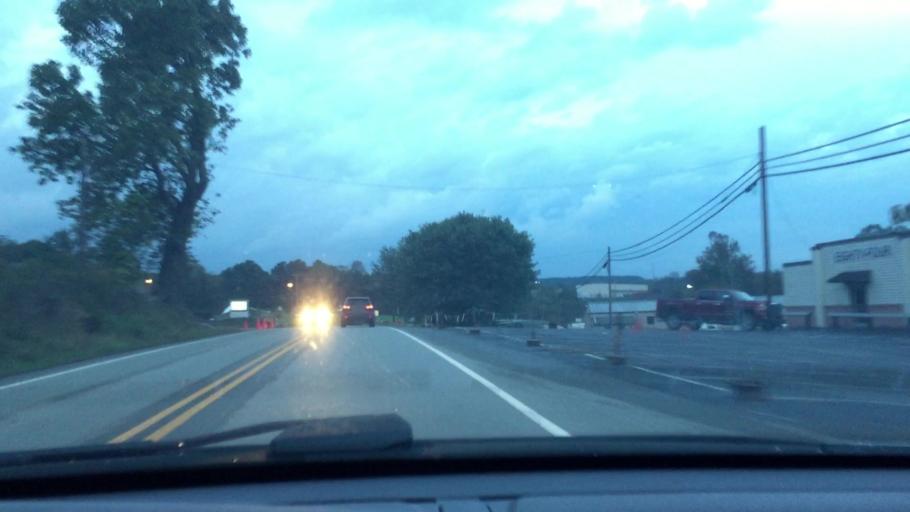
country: US
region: Pennsylvania
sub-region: Washington County
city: McGovern
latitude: 40.1859
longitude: -80.1553
